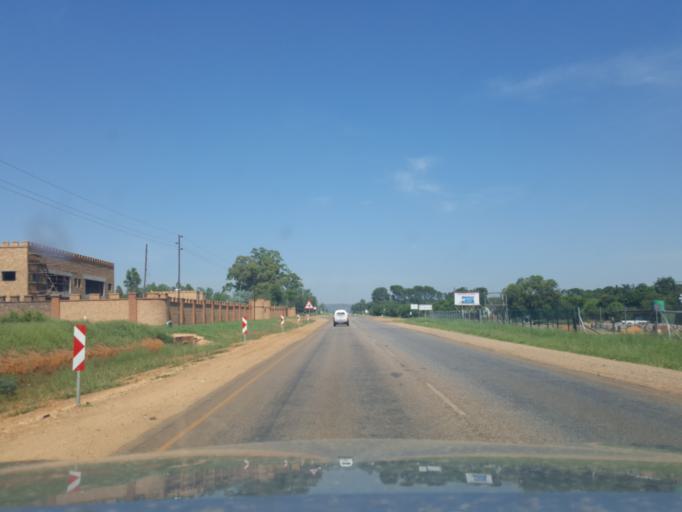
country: ZA
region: Gauteng
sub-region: City of Tshwane Metropolitan Municipality
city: Pretoria
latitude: -25.6793
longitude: 28.3189
